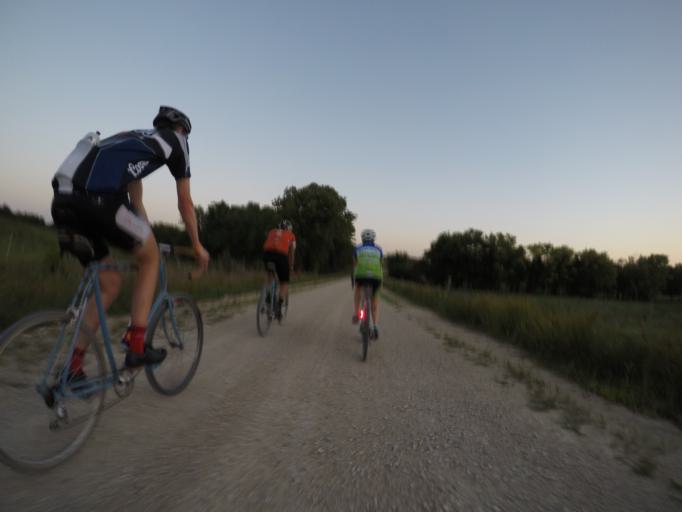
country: US
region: Kansas
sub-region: Riley County
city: Ogden
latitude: 38.9857
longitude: -96.5602
